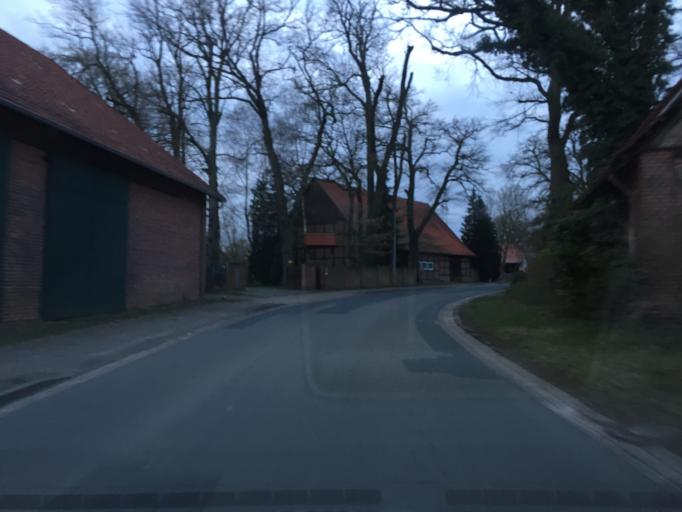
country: DE
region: Lower Saxony
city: Steimbke
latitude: 52.5987
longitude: 9.3962
